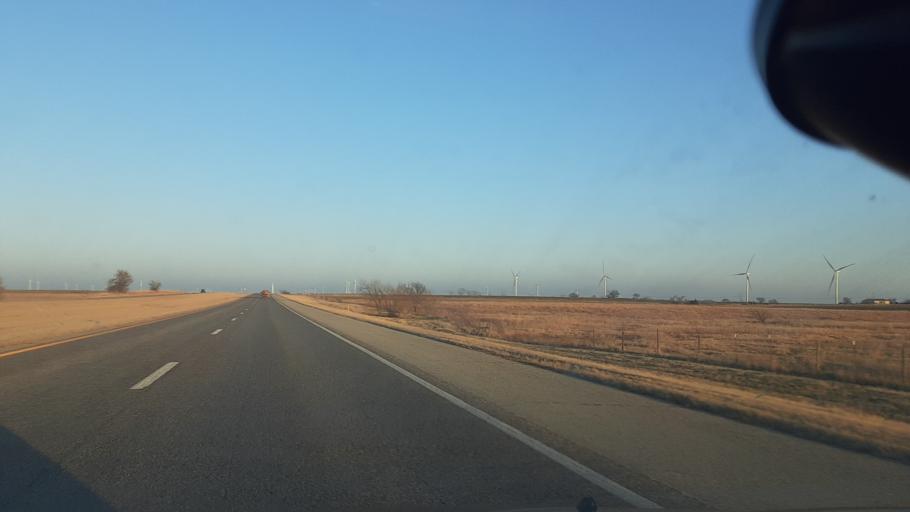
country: US
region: Oklahoma
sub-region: Noble County
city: Perry
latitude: 36.3975
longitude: -97.5023
